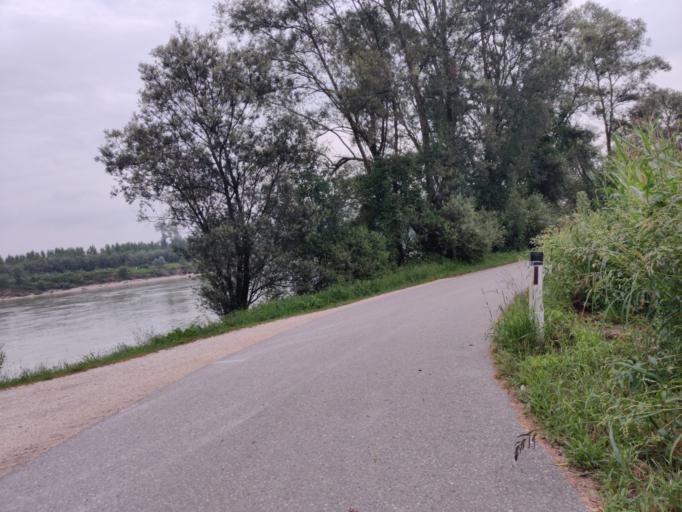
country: AT
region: Upper Austria
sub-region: Politischer Bezirk Linz-Land
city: Enns
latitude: 48.2339
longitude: 14.4573
